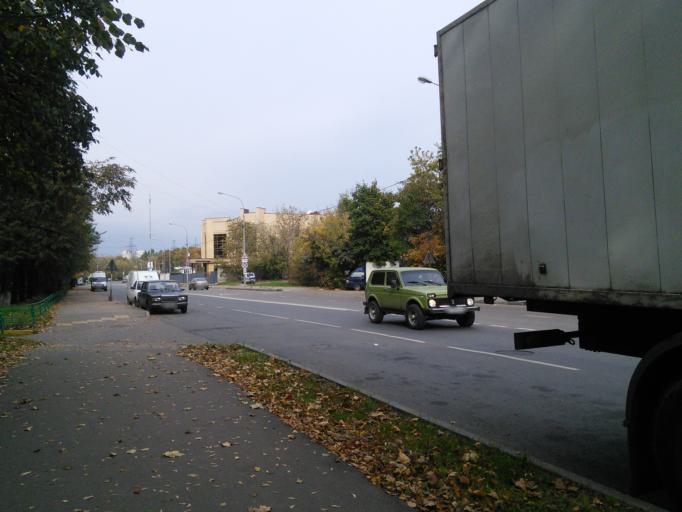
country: RU
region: Moskovskaya
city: Levoberezhnaya
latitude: 55.8720
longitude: 37.4701
